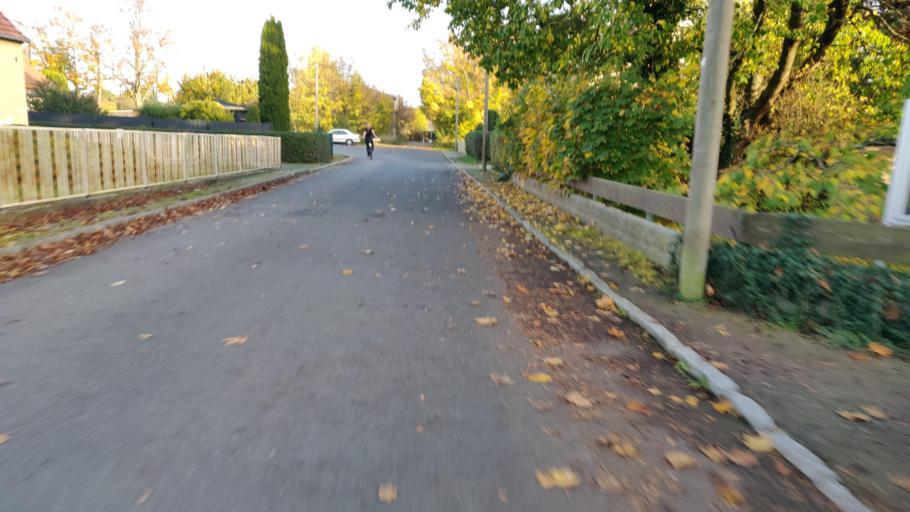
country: DE
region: Brandenburg
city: Grossthiemig
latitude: 51.3530
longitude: 13.6936
